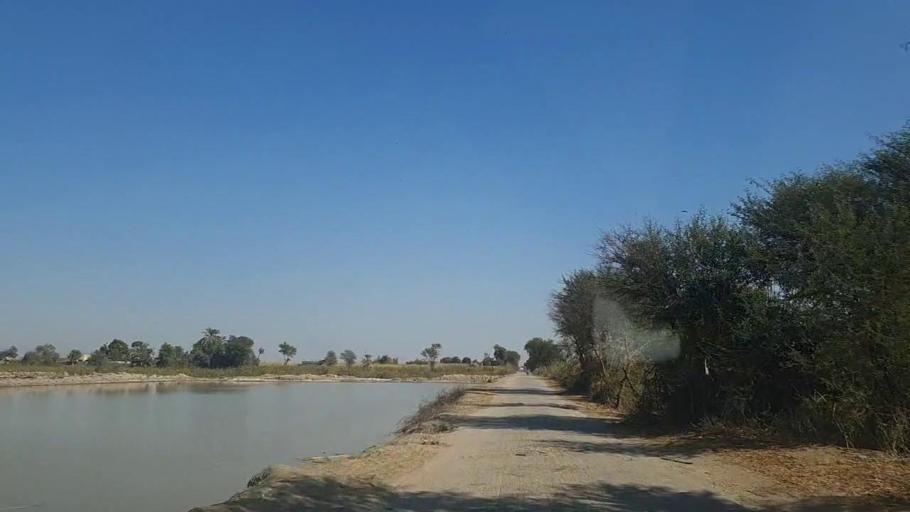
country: PK
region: Sindh
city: Sanghar
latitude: 26.2207
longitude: 68.9434
